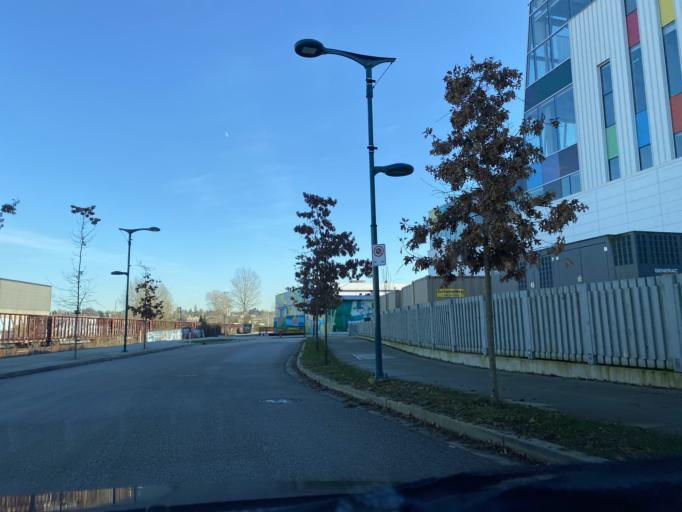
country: CA
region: British Columbia
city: Vancouver
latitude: 49.2680
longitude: -123.0917
